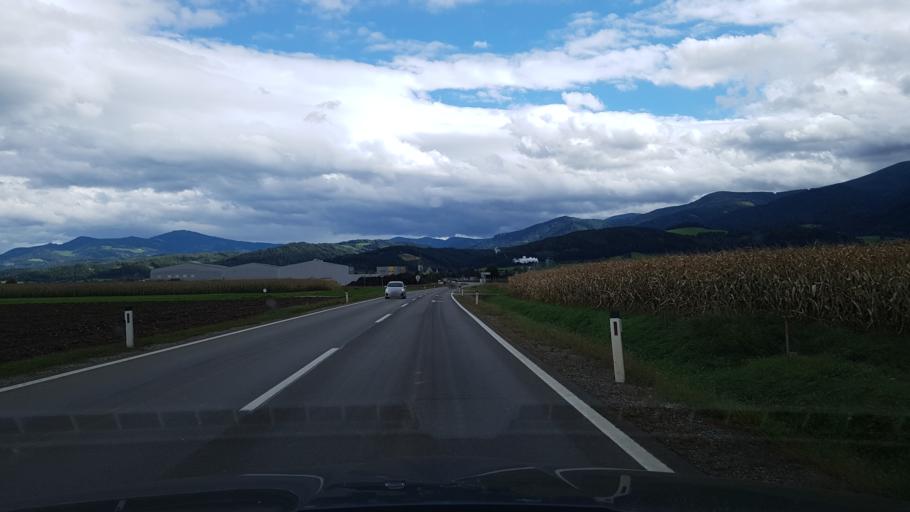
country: AT
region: Styria
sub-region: Politischer Bezirk Murtal
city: Weisskirchen in Steiermark
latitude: 47.1585
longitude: 14.7178
